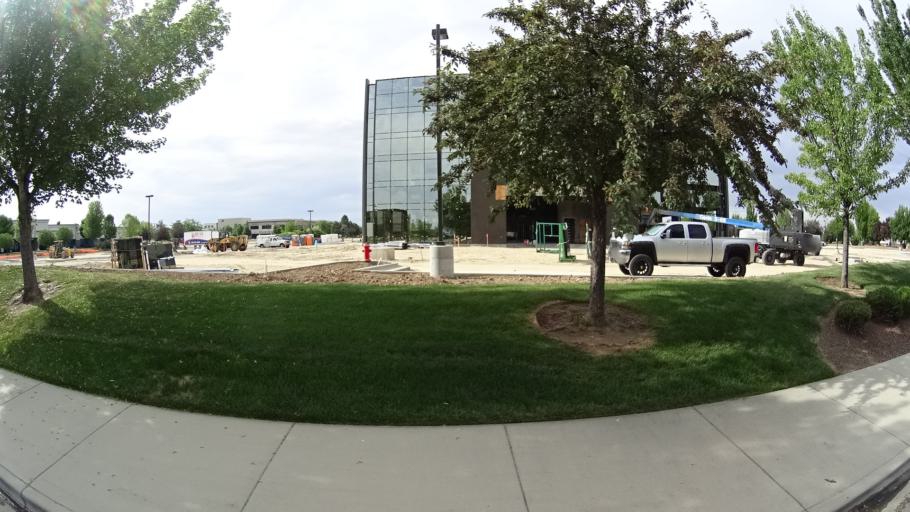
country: US
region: Idaho
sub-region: Ada County
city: Meridian
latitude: 43.5886
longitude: -116.3508
